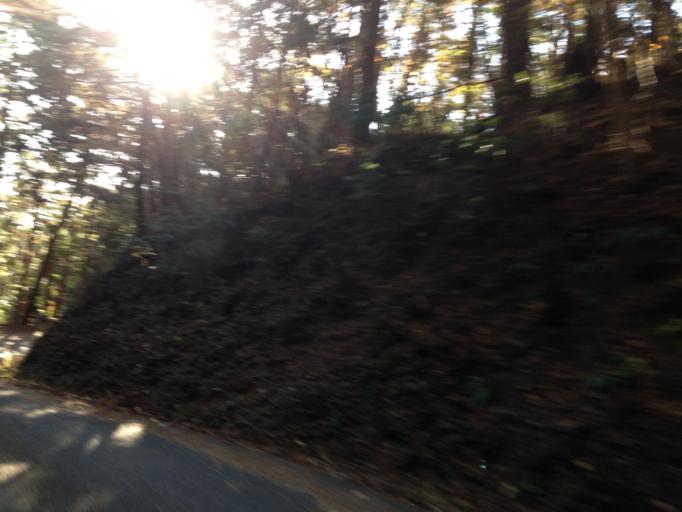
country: JP
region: Gifu
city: Mitake
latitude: 35.6130
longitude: 137.2128
